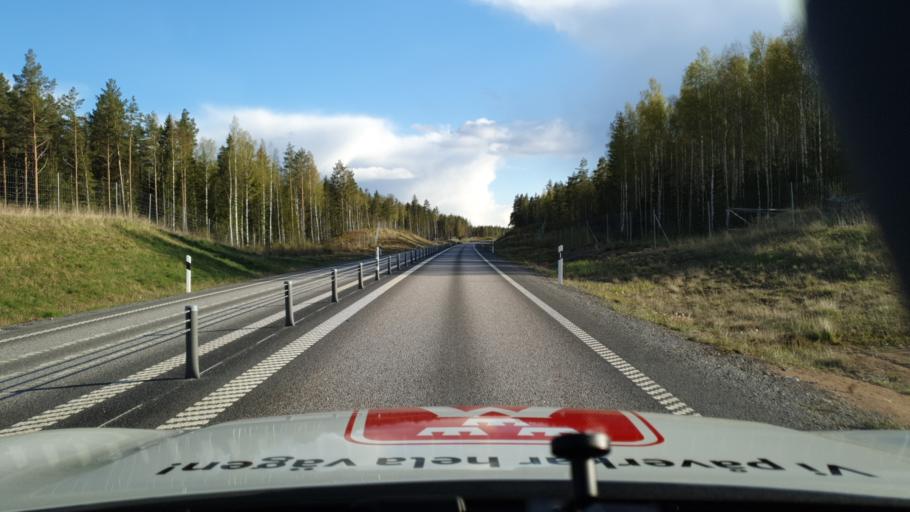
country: SE
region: Uppsala
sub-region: Heby Kommun
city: Tarnsjo
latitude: 60.0833
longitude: 16.9161
